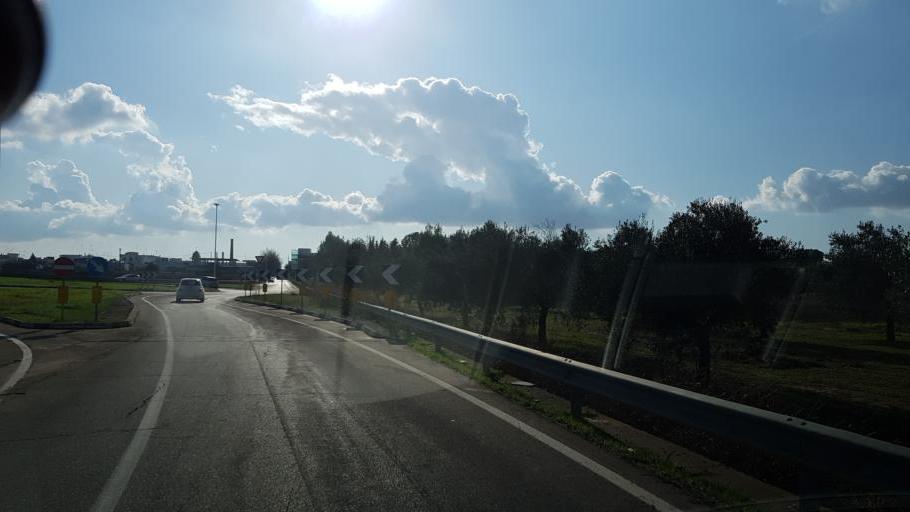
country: IT
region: Apulia
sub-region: Provincia di Lecce
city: Salice Salentino
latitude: 40.3914
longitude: 17.9682
